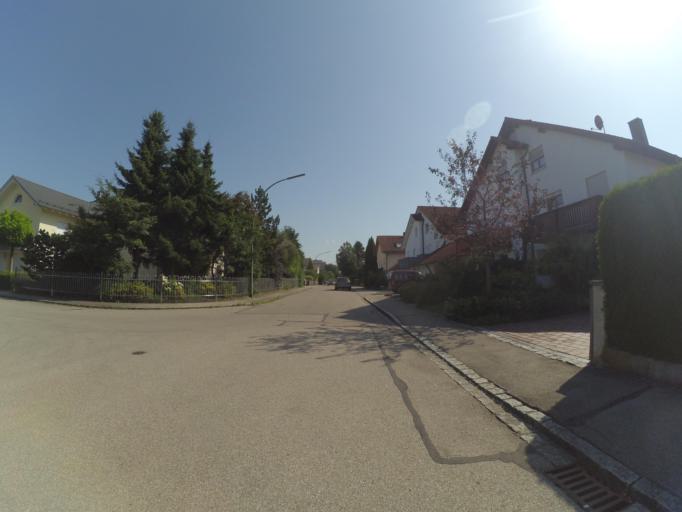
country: DE
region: Bavaria
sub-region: Swabia
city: Buchloe
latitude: 48.0372
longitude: 10.7102
